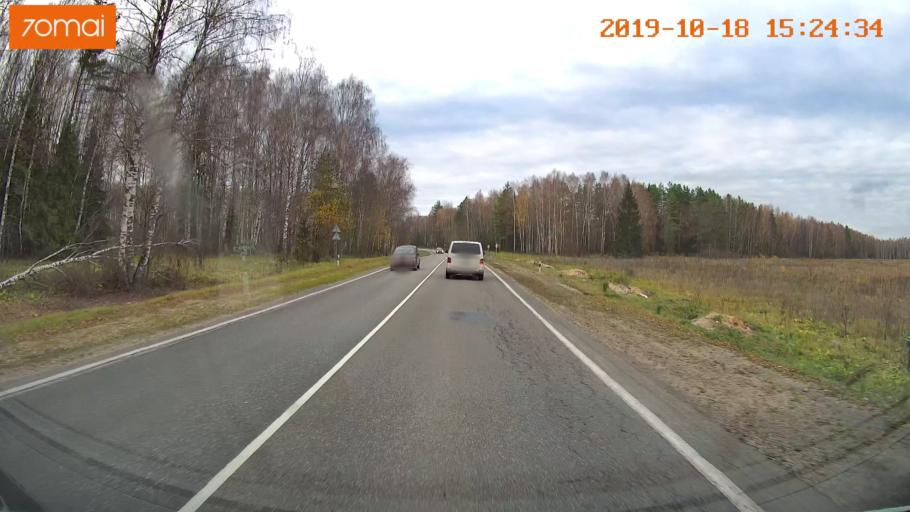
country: RU
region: Vladimir
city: Anopino
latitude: 55.7355
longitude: 40.7211
